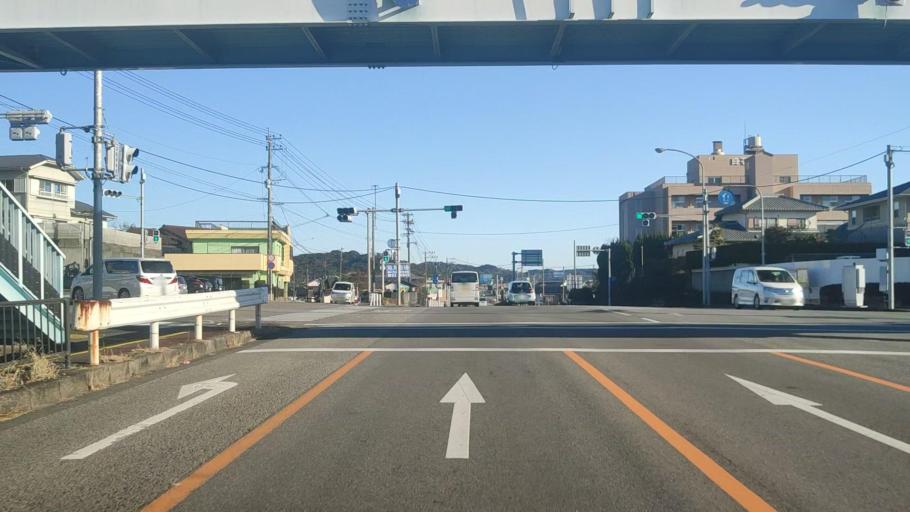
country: JP
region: Miyazaki
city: Nobeoka
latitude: 32.4727
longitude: 131.6516
